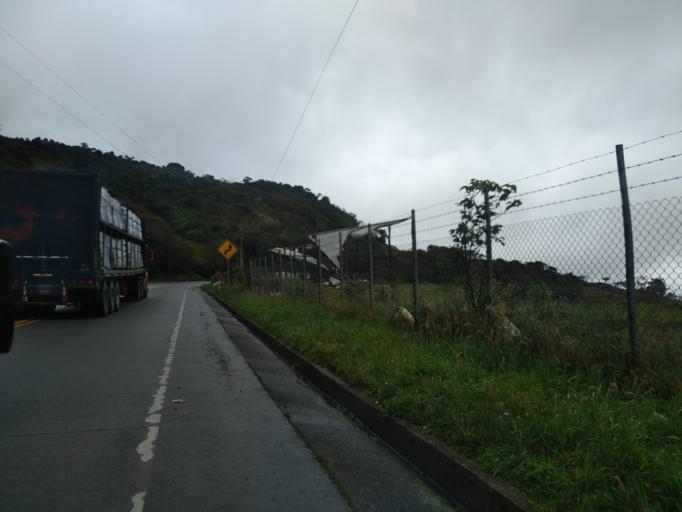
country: EC
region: Loja
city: Catamayo
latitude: -3.8610
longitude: -79.2831
